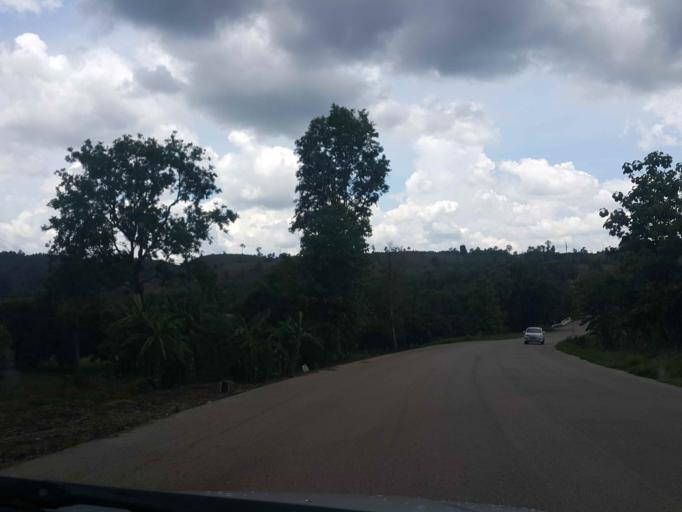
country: TH
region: Phayao
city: Dok Kham Tai
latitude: 18.9691
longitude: 100.0746
